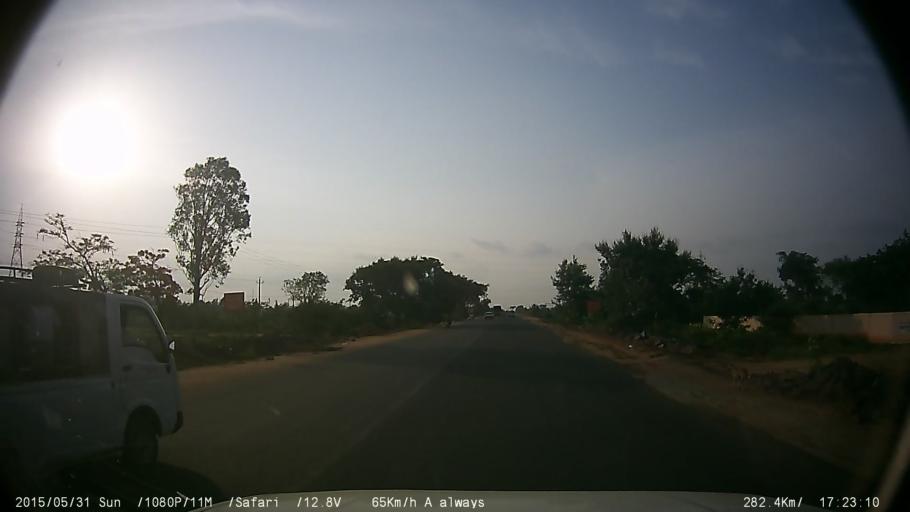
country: IN
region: Karnataka
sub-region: Chamrajnagar
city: Gundlupet
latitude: 11.8373
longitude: 76.6754
